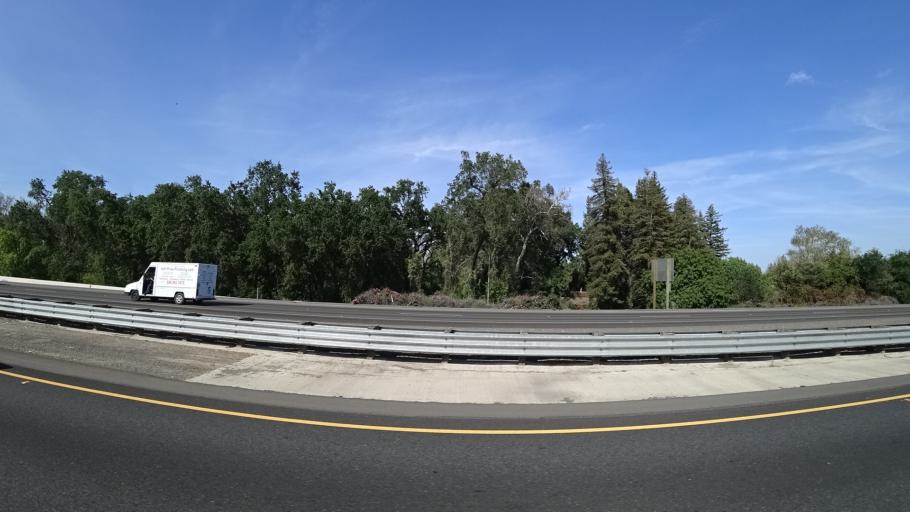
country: US
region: California
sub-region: Butte County
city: Chico
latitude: 39.7372
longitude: -121.8208
